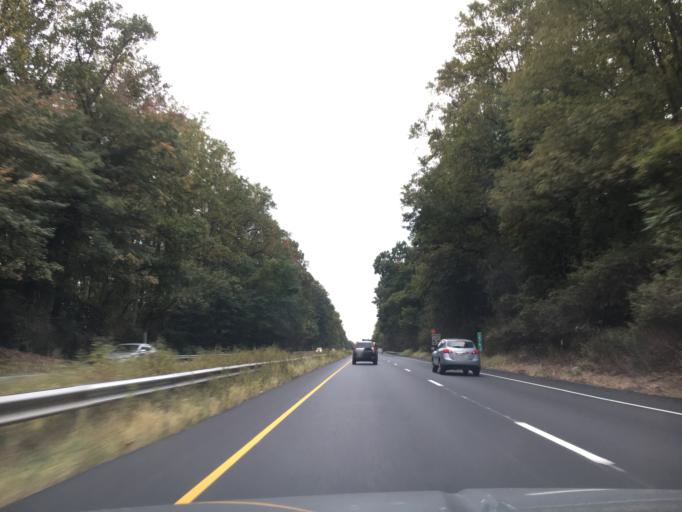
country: US
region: Pennsylvania
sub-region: Chester County
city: Thorndale
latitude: 40.0069
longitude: -75.7541
